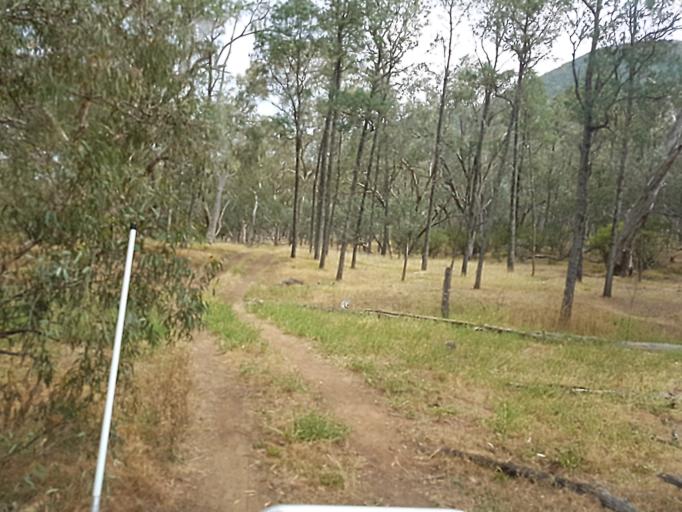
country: AU
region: New South Wales
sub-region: Snowy River
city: Jindabyne
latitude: -36.9637
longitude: 148.4129
